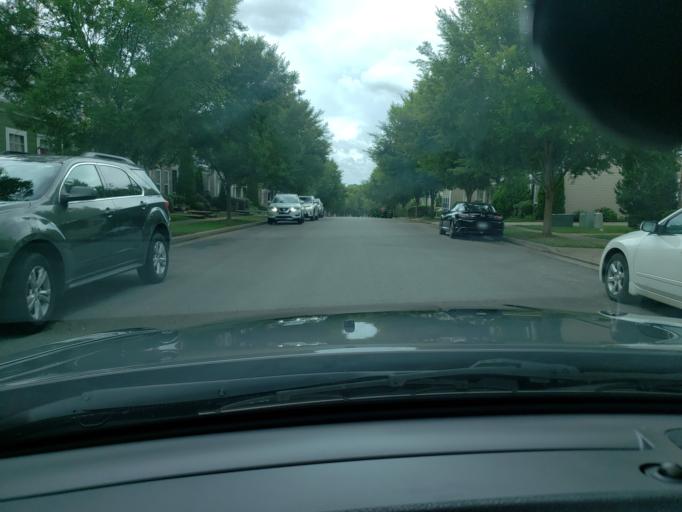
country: US
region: Tennessee
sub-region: Williamson County
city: Brentwood Estates
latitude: 36.0223
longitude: -86.7023
